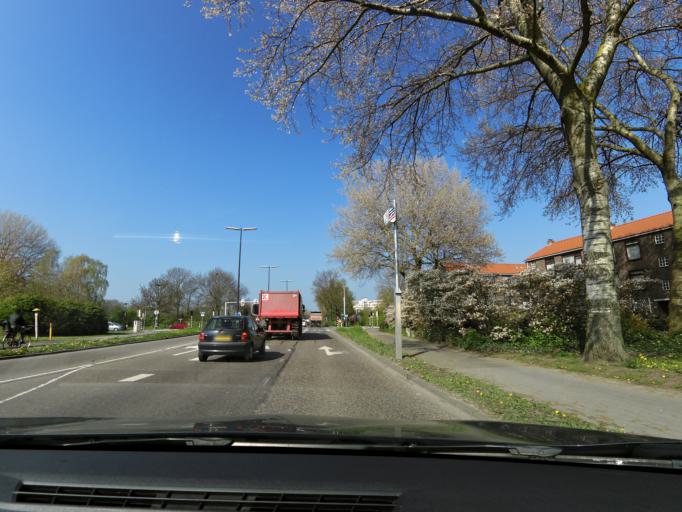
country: NL
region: South Holland
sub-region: Gemeente Vlaardingen
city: Vlaardingen
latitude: 51.9123
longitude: 4.3273
